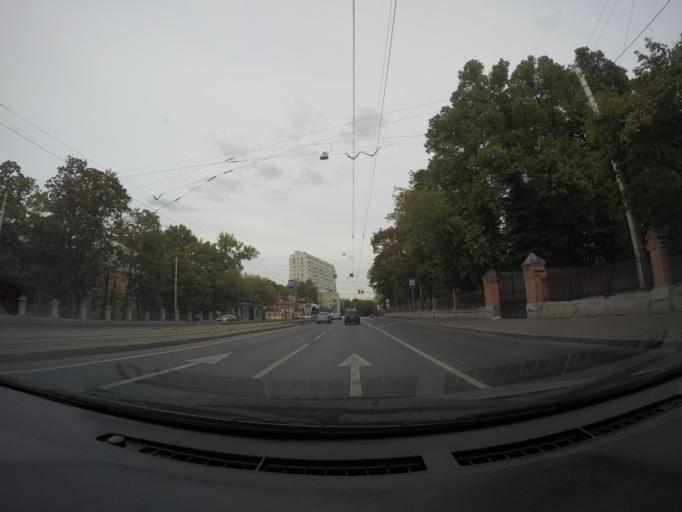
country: RU
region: Moscow
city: Sokol'niki
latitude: 55.7889
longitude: 37.6905
